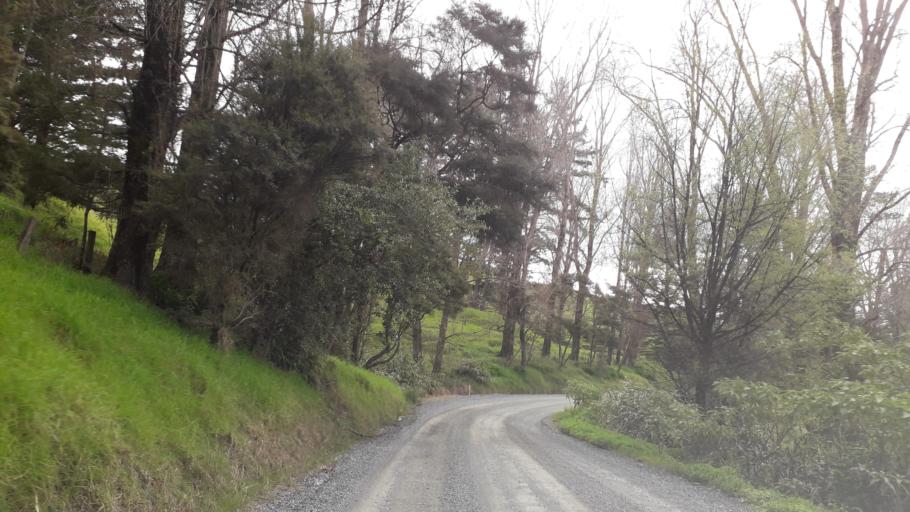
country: NZ
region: Northland
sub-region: Far North District
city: Taipa
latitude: -35.0925
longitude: 173.5163
